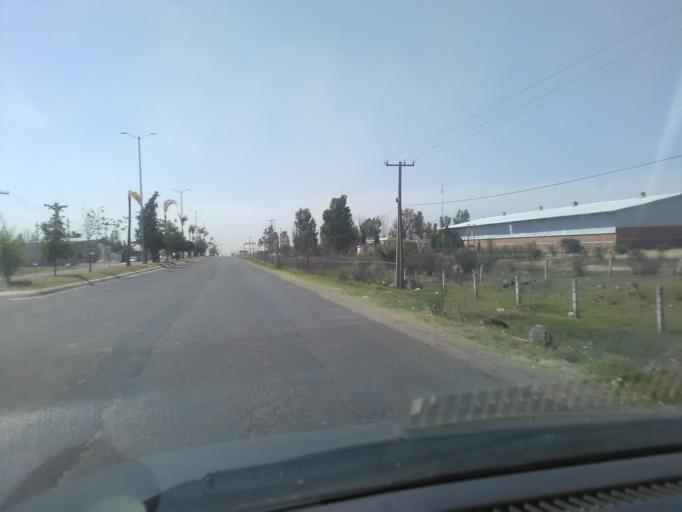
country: MX
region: Durango
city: Victoria de Durango
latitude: 24.0281
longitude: -104.5895
